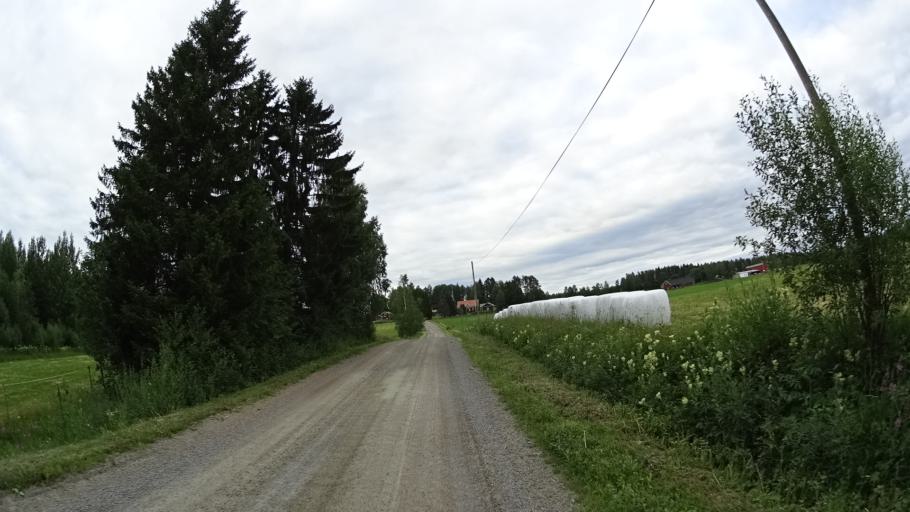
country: FI
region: Satakunta
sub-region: Pohjois-Satakunta
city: Jaemijaervi
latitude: 61.7775
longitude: 22.8753
